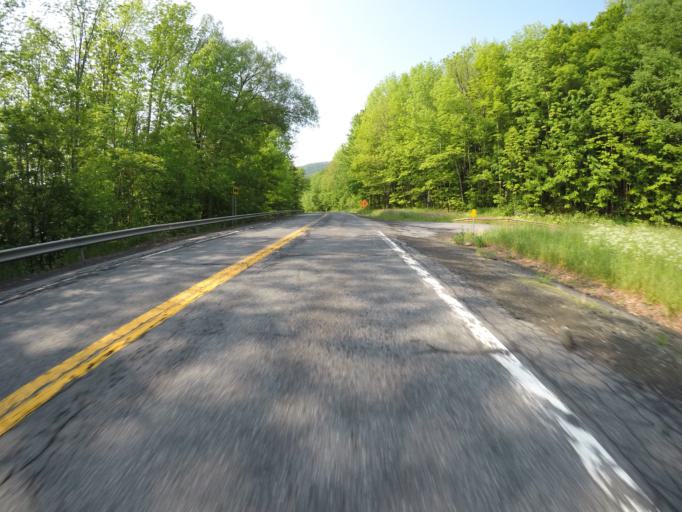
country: US
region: New York
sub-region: Sullivan County
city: Livingston Manor
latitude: 42.0957
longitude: -74.7993
